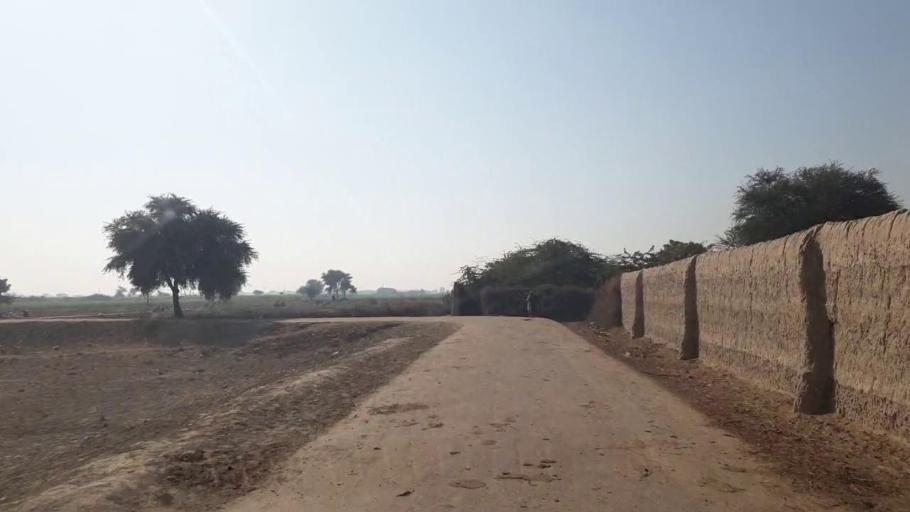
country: PK
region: Sindh
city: Shahpur Chakar
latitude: 26.0719
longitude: 68.5959
